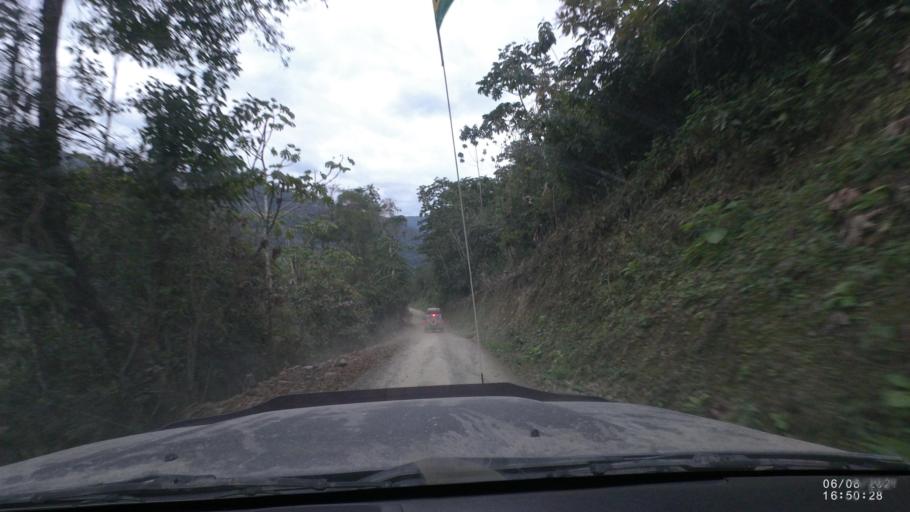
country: BO
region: La Paz
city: Quime
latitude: -16.4990
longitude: -66.7714
